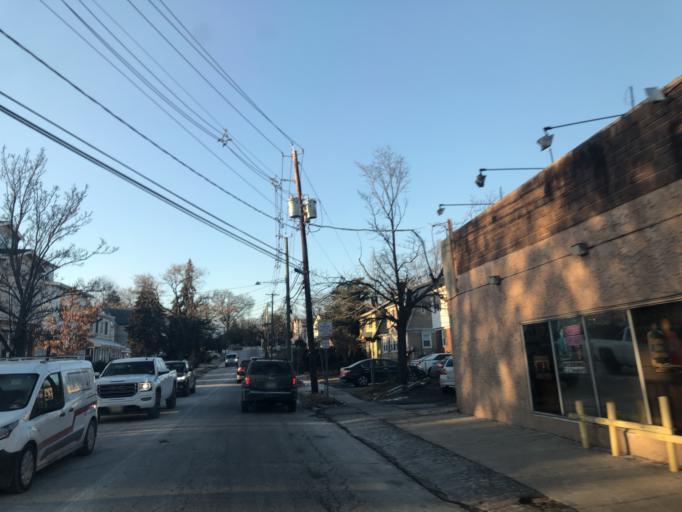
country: US
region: New Jersey
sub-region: Union County
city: Union
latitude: 40.7152
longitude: -74.2528
